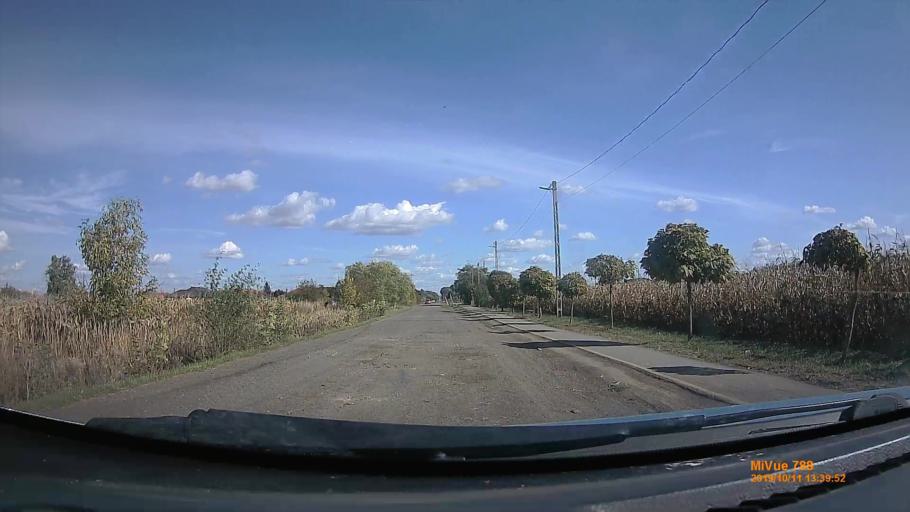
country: HU
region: Hajdu-Bihar
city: Balmazujvaros
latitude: 47.5399
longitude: 21.3333
